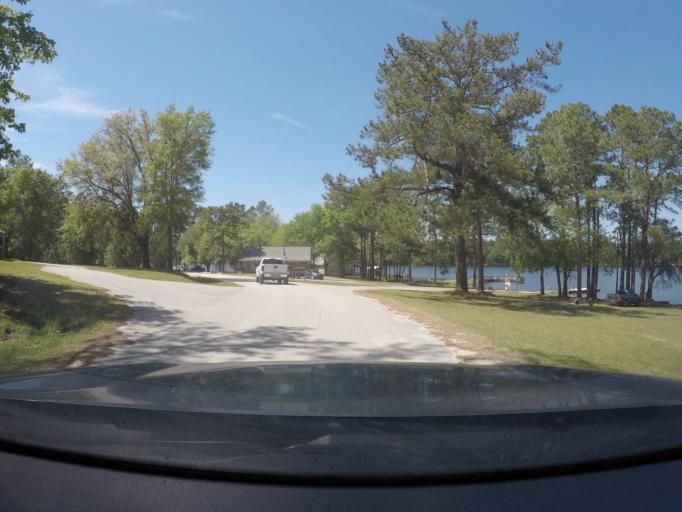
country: US
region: Georgia
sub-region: Evans County
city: Claxton
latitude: 32.1279
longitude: -81.7933
